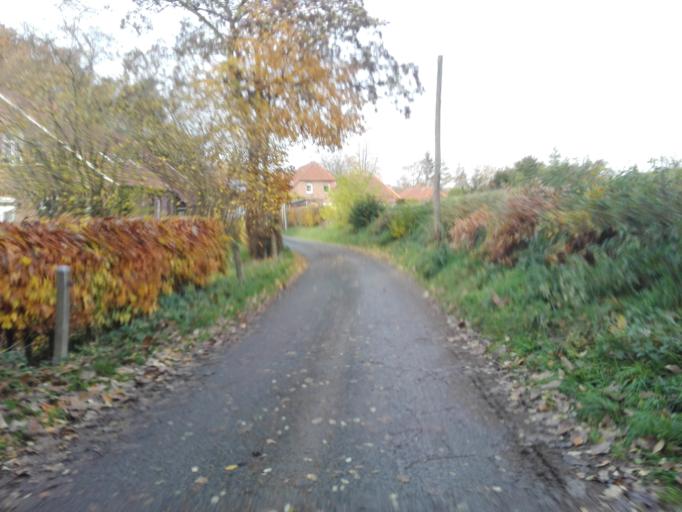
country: DE
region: Lower Saxony
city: Wiefelstede
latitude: 53.2786
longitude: 8.1466
